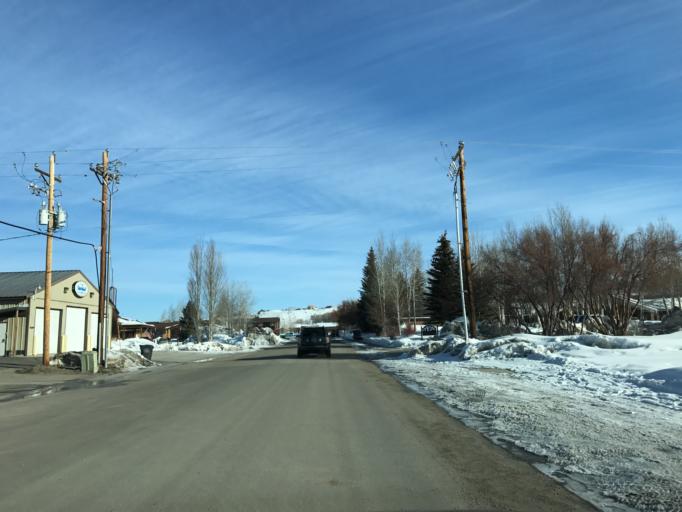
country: US
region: Wyoming
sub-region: Sublette County
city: Pinedale
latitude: 42.8677
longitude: -109.8572
